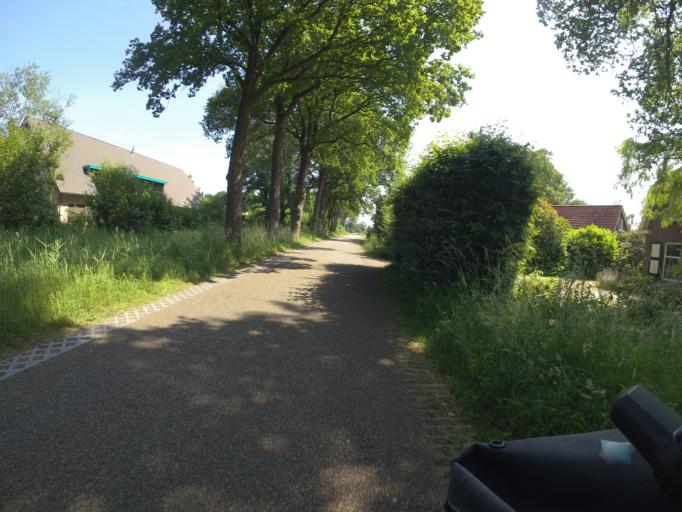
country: NL
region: Gelderland
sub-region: Berkelland
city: Neede
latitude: 52.1277
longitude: 6.6337
